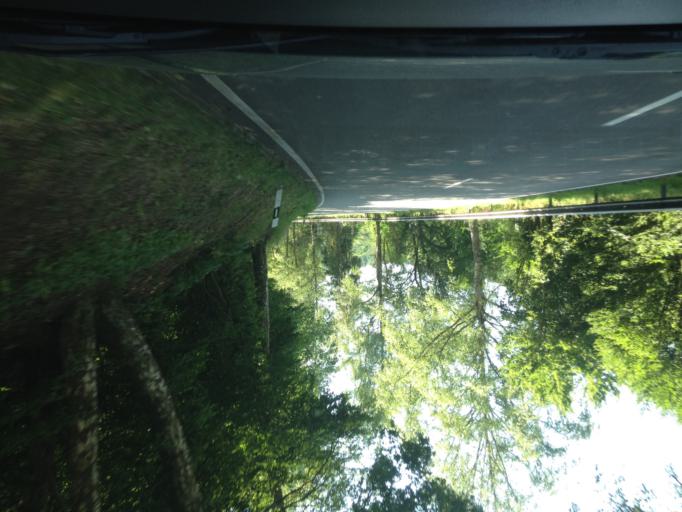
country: DE
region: Rheinland-Pfalz
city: Frankenstein
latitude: 49.4461
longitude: 7.9922
